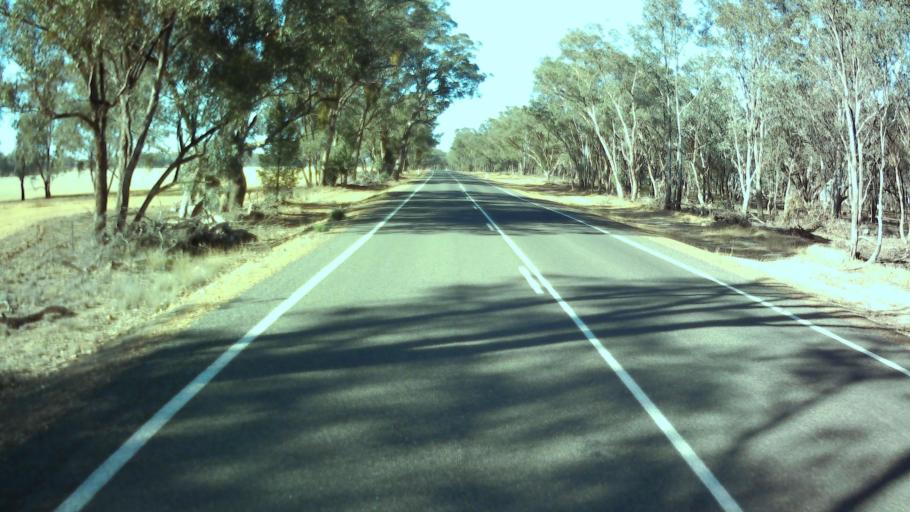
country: AU
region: New South Wales
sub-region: Weddin
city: Grenfell
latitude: -34.0037
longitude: 148.1253
